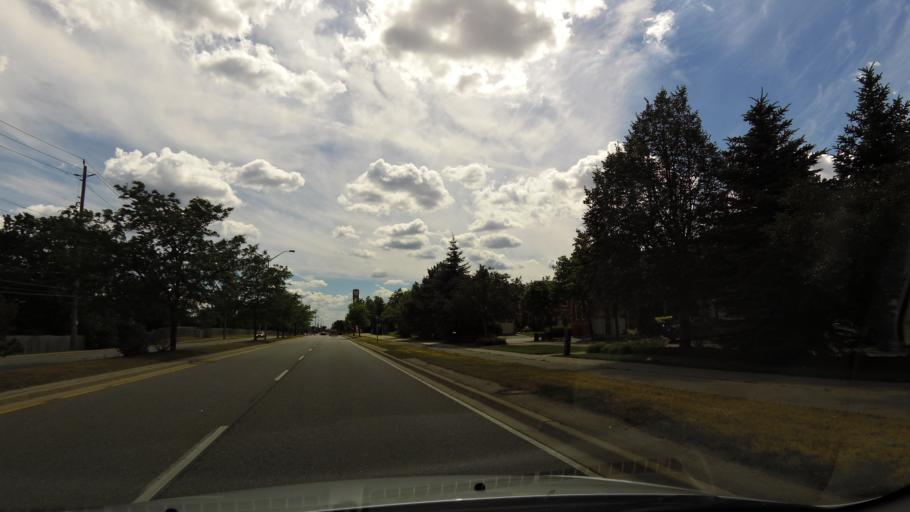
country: CA
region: Ontario
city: Oakville
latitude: 43.4843
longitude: -79.6916
